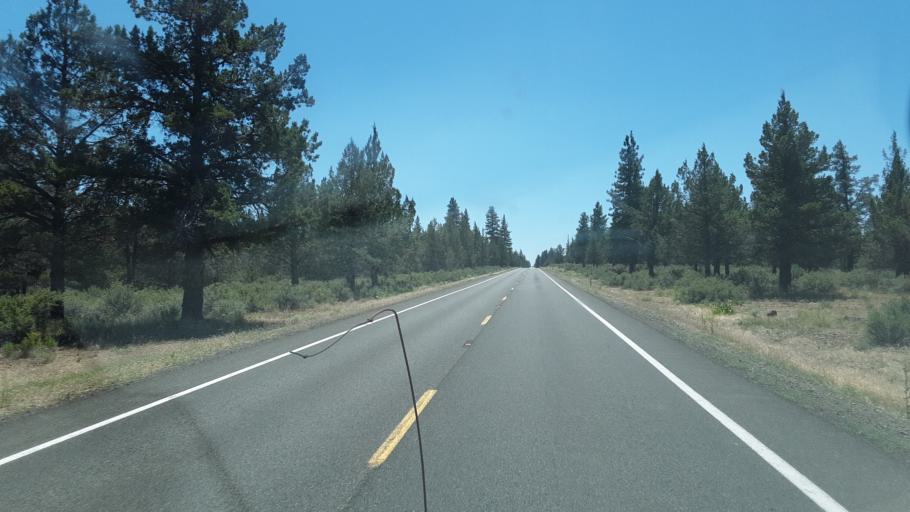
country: US
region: California
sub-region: Siskiyou County
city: Tulelake
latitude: 41.6348
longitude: -121.2301
